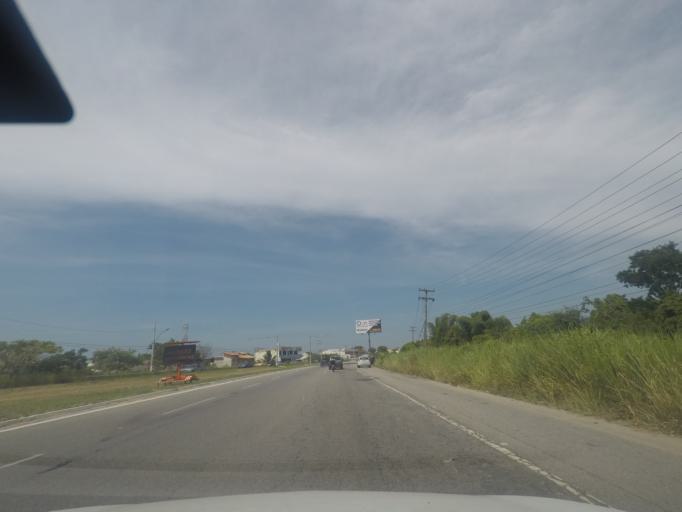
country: BR
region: Rio de Janeiro
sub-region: Marica
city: Marica
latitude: -22.9066
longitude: -42.8180
